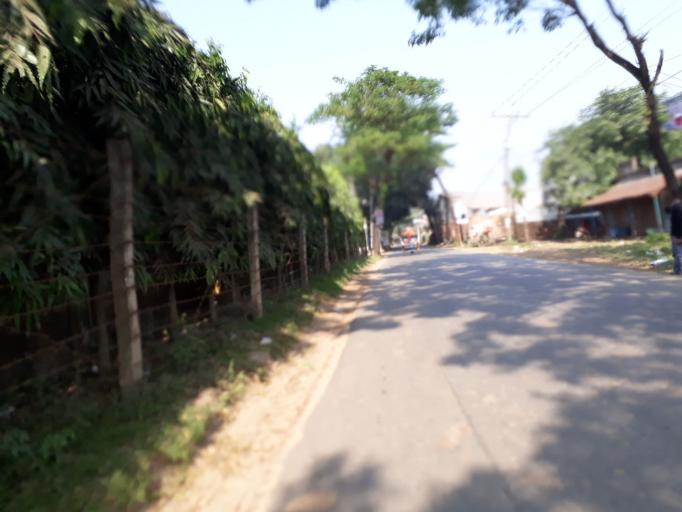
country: BD
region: Dhaka
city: Tungi
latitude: 23.8649
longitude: 90.3106
